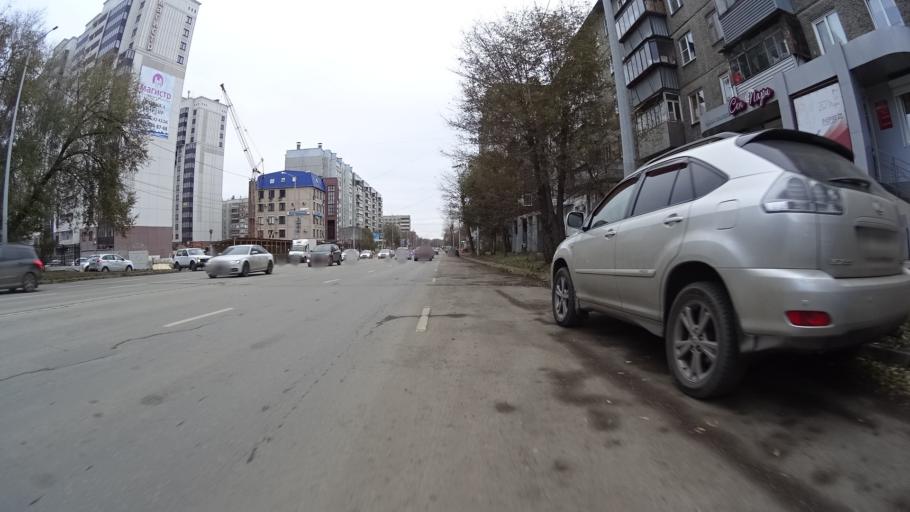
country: RU
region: Chelyabinsk
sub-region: Gorod Chelyabinsk
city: Chelyabinsk
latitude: 55.1578
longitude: 61.4168
